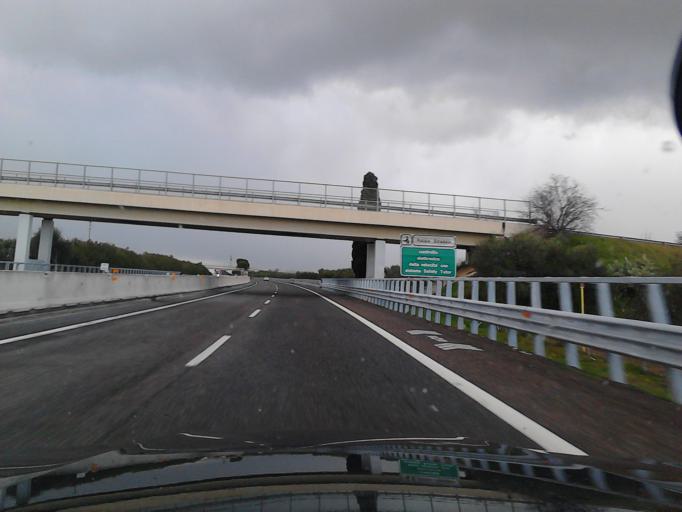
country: IT
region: Apulia
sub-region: Provincia di Bari
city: Bitonto
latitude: 41.1338
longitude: 16.7103
